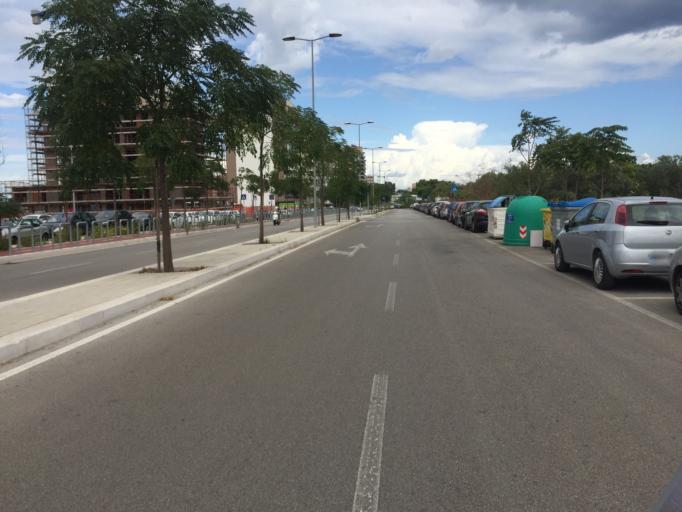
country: IT
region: Apulia
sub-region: Provincia di Bari
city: Bari
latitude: 41.1042
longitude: 16.8538
